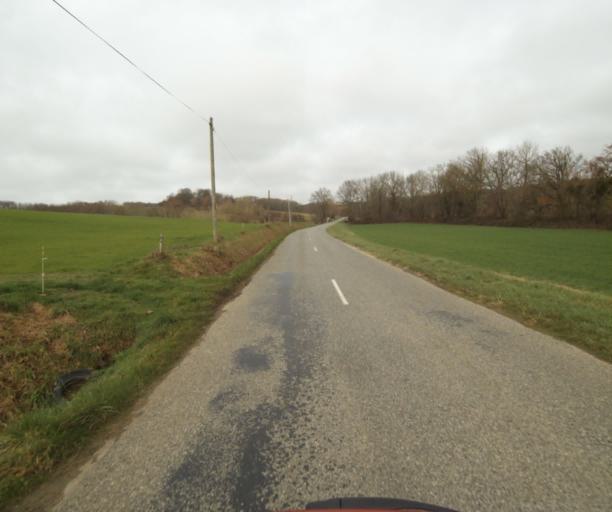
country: FR
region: Midi-Pyrenees
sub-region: Departement de l'Ariege
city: Pamiers
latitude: 43.1413
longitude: 1.5323
